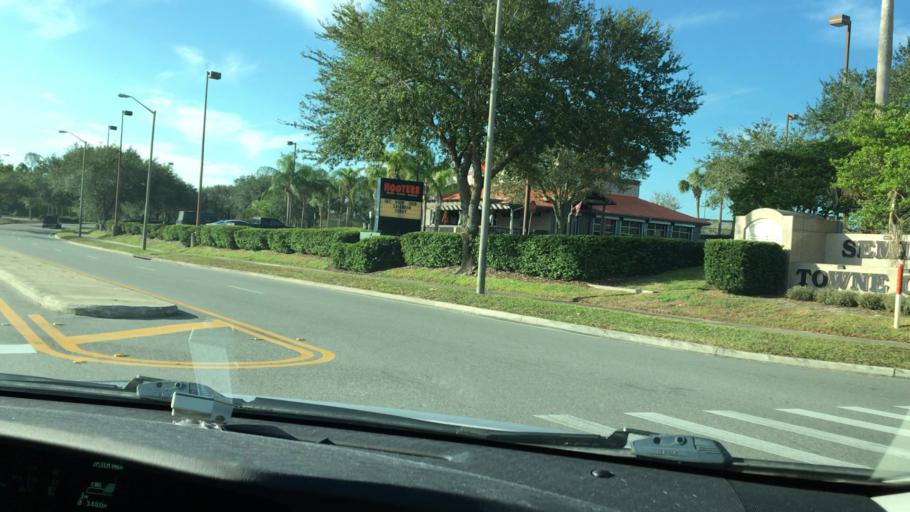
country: US
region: Florida
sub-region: Seminole County
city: Lake Mary
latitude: 28.8057
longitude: -81.3351
